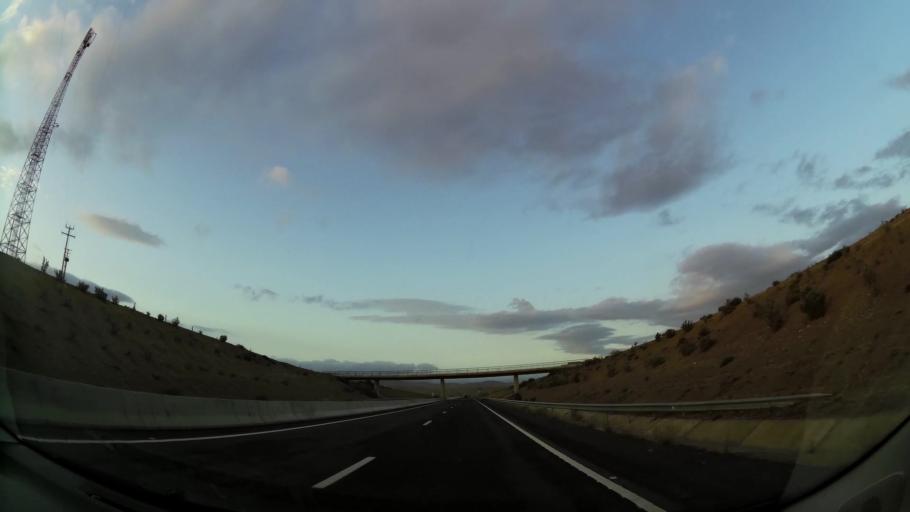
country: MA
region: Oriental
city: Taourirt
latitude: 34.5588
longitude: -2.8400
